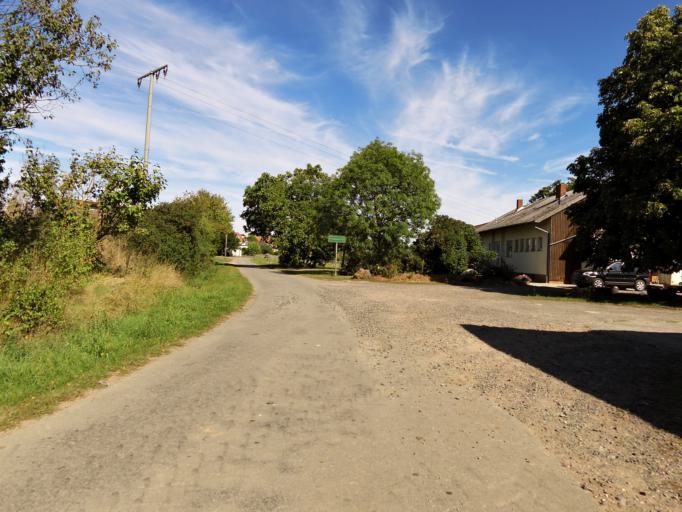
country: DE
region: Rheinland-Pfalz
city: Standenbuhl
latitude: 49.5920
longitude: 7.9763
